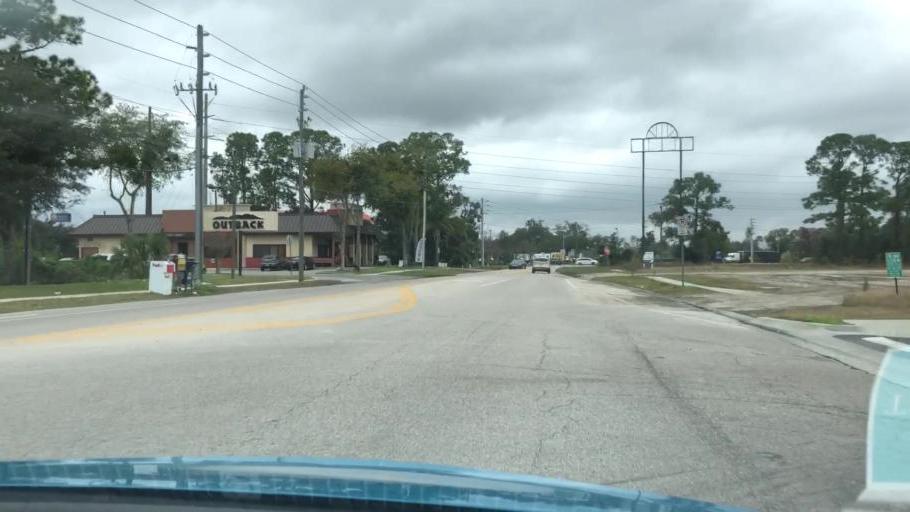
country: US
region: Florida
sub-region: Seminole County
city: Lake Mary
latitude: 28.8126
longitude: -81.3342
